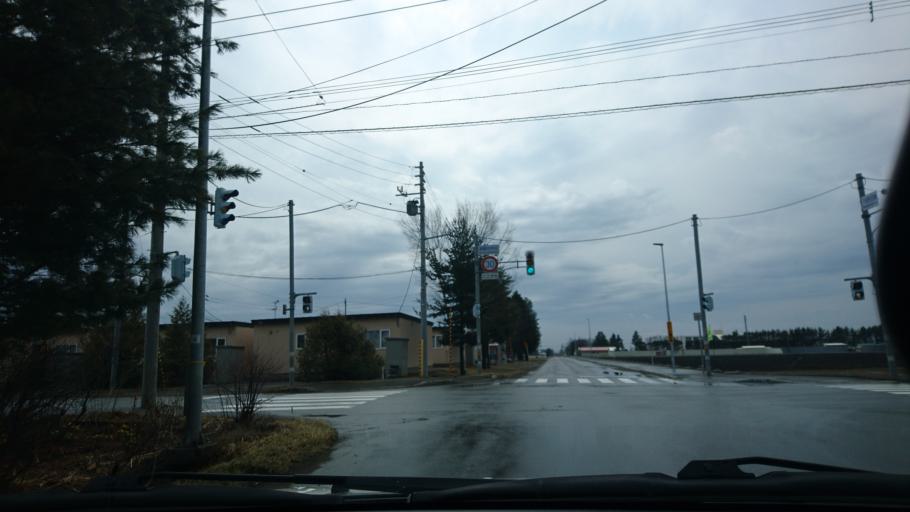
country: JP
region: Hokkaido
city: Otofuke
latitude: 42.9714
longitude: 143.1920
